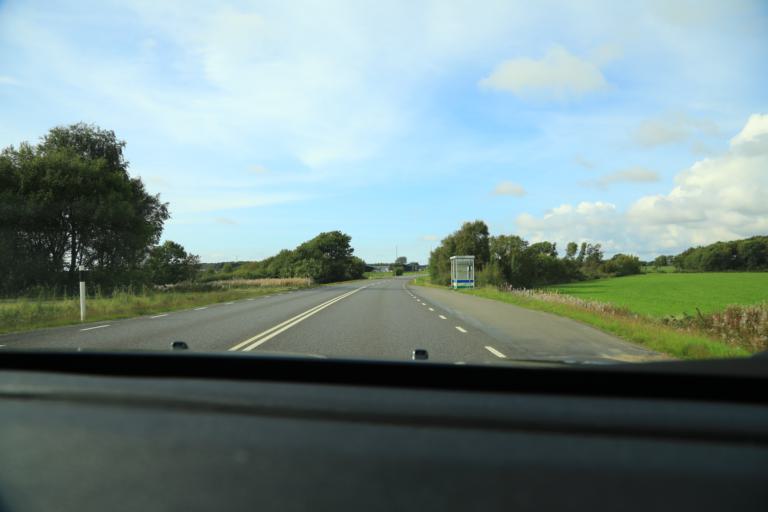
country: SE
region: Halland
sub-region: Varbergs Kommun
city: Traslovslage
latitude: 57.0511
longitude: 12.3063
